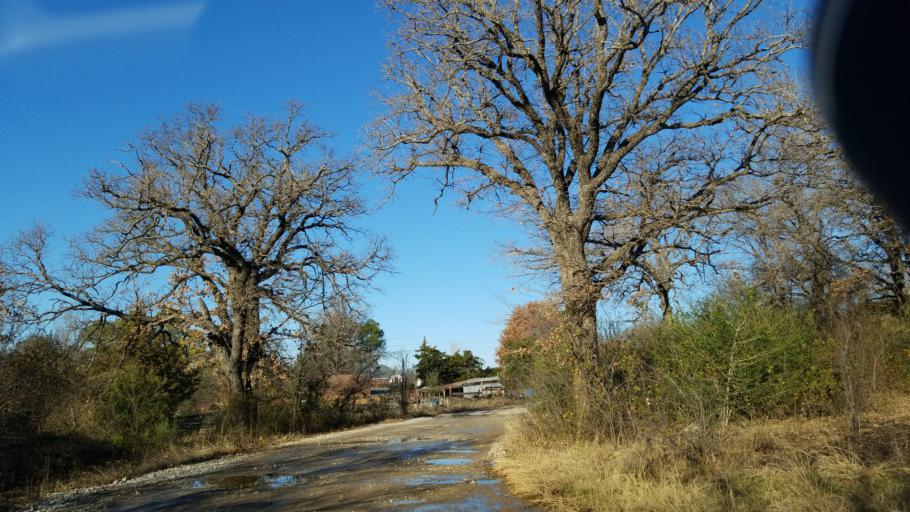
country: US
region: Texas
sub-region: Denton County
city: Corinth
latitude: 33.1566
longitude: -97.0928
